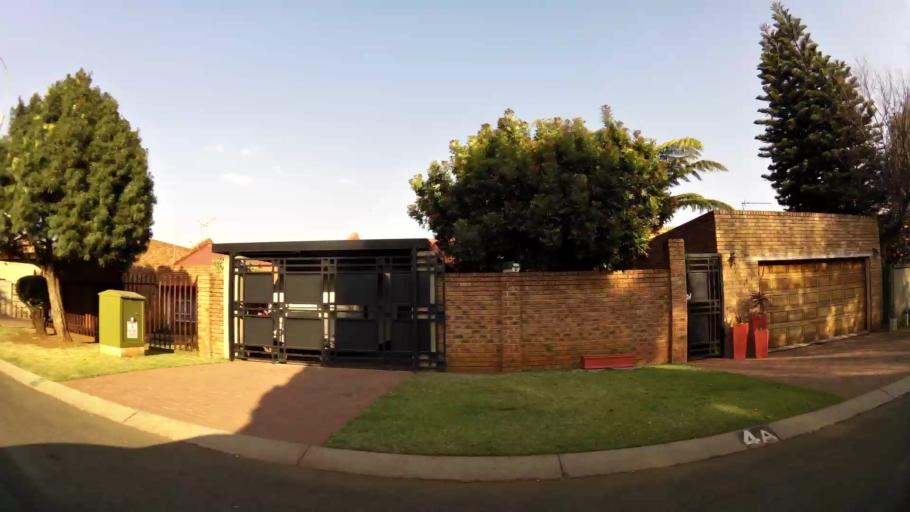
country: ZA
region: Gauteng
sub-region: City of Johannesburg Metropolitan Municipality
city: Modderfontein
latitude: -26.0709
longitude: 28.2103
